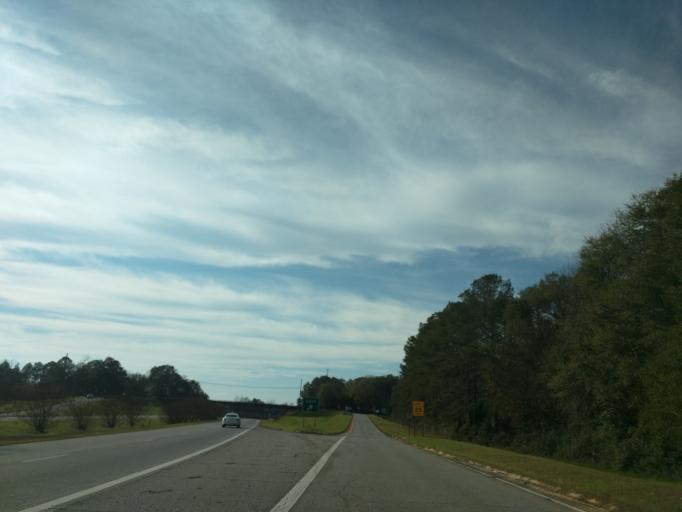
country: US
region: Georgia
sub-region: Decatur County
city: Bainbridge
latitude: 30.8923
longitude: -84.5734
